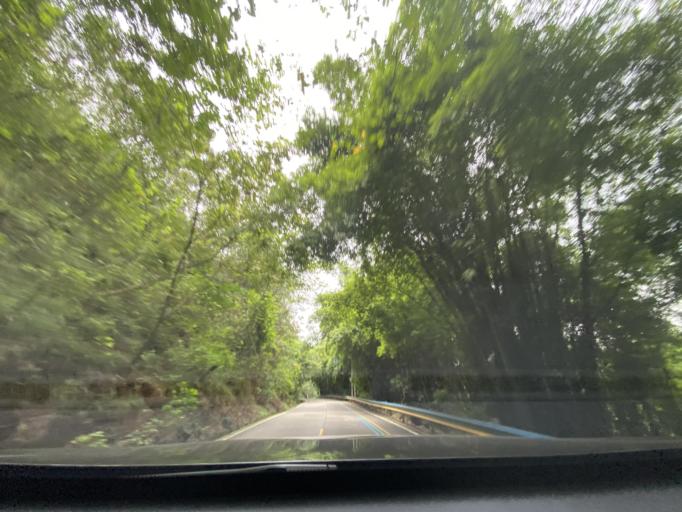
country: CN
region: Sichuan
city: Dongsheng
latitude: 30.4066
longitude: 104.0042
